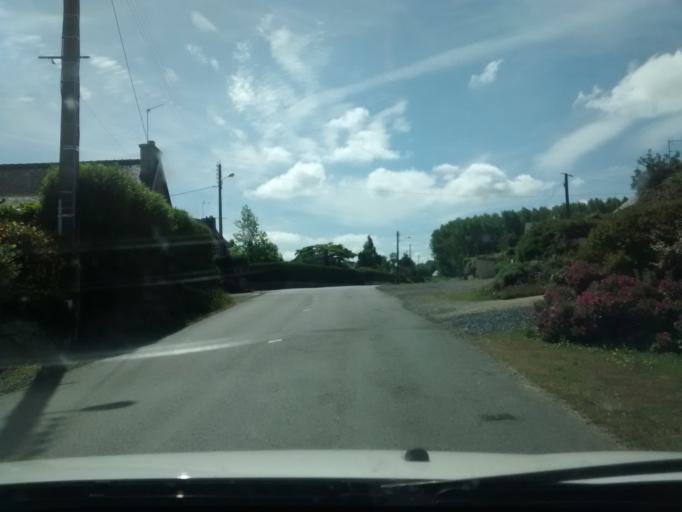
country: FR
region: Brittany
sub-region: Departement des Cotes-d'Armor
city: Penvenan
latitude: 48.8232
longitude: -3.3015
